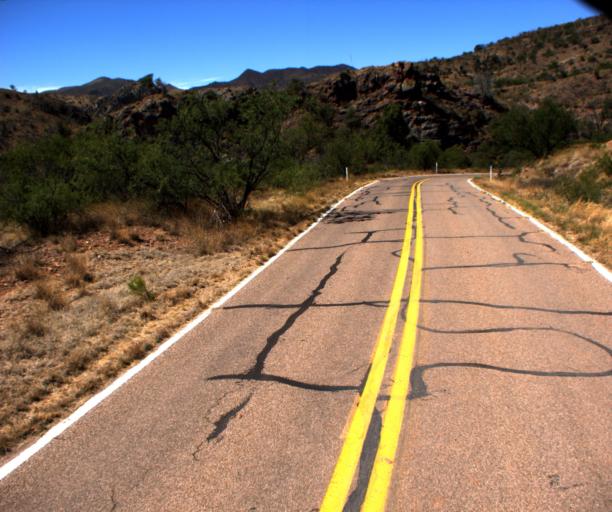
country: US
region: Arizona
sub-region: Santa Cruz County
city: Rio Rico
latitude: 31.4013
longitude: -111.0900
